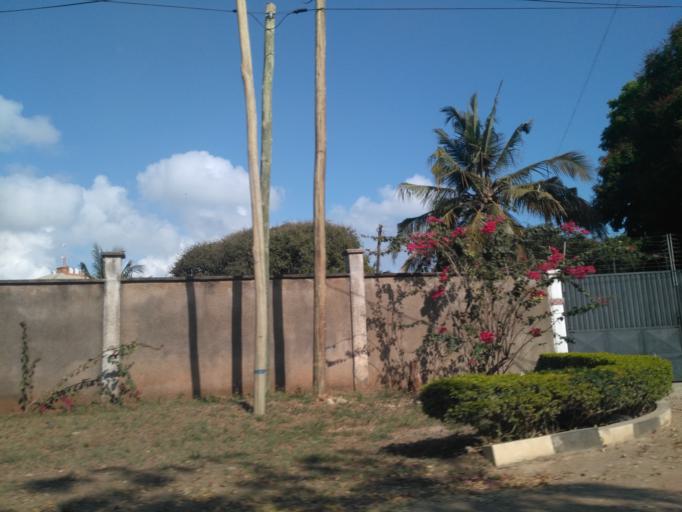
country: TZ
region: Dar es Salaam
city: Magomeni
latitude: -6.7454
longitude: 39.2836
